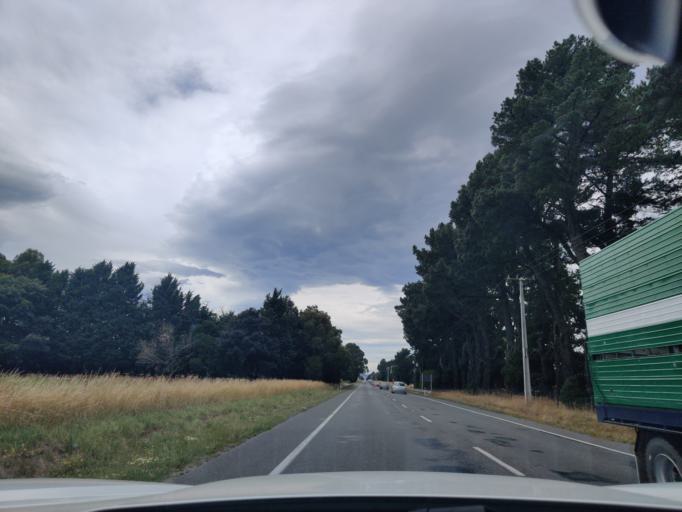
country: NZ
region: Wellington
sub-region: Masterton District
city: Masterton
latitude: -40.9859
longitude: 175.5778
